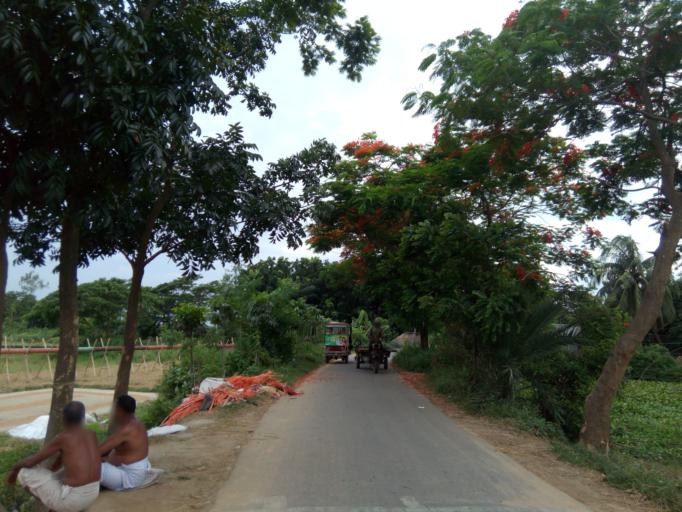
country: BD
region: Dhaka
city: Paltan
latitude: 23.7475
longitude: 90.4811
